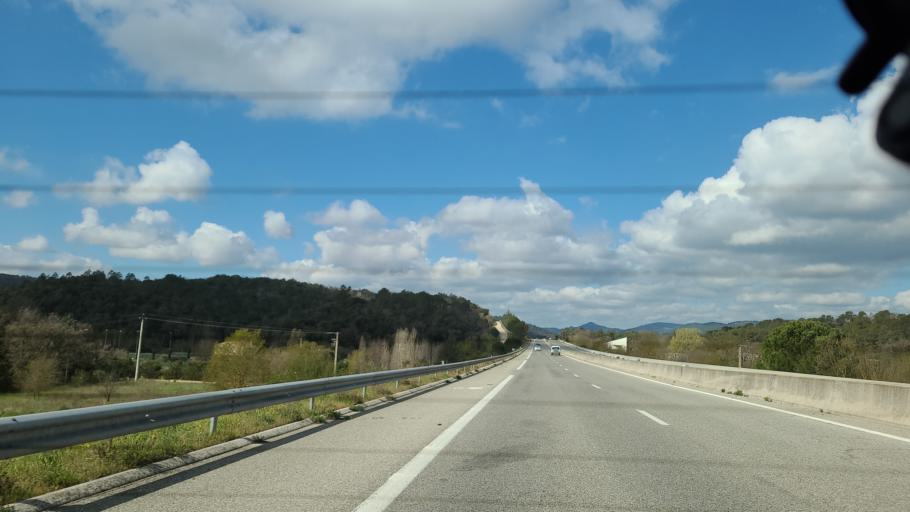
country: FR
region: Provence-Alpes-Cote d'Azur
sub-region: Departement du Var
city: Pignans
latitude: 43.2888
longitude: 6.2322
